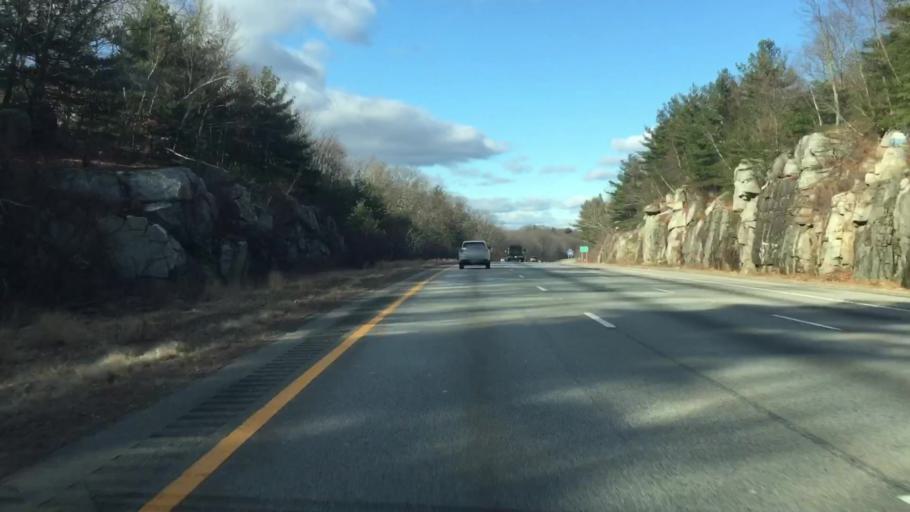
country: US
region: Massachusetts
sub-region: Middlesex County
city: Hopkinton
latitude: 42.1884
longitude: -71.5342
